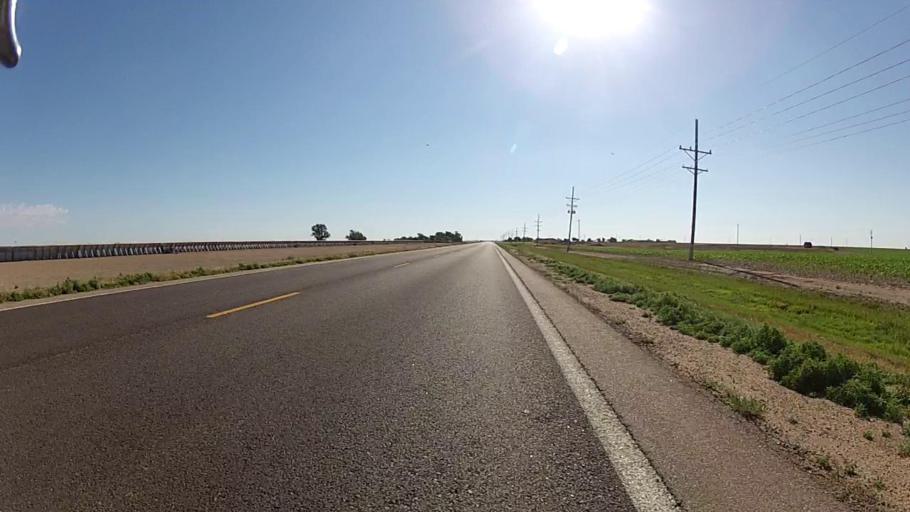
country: US
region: Kansas
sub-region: Haskell County
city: Sublette
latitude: 37.5445
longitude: -100.6232
